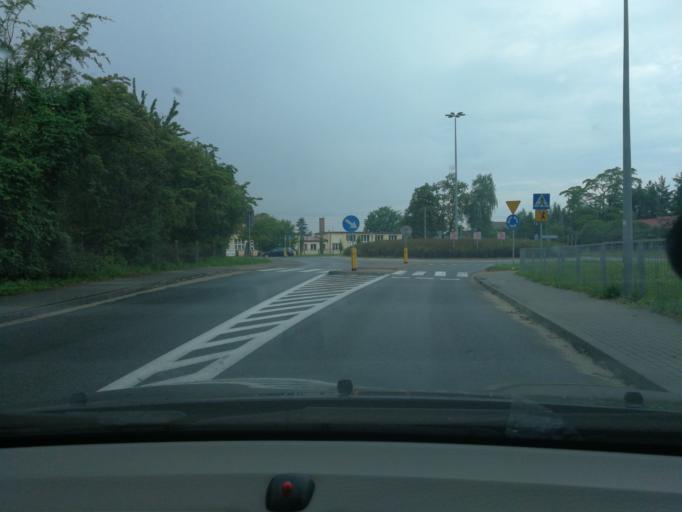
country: PL
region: Masovian Voivodeship
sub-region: Powiat zyrardowski
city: Radziejowice
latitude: 52.0038
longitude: 20.5565
